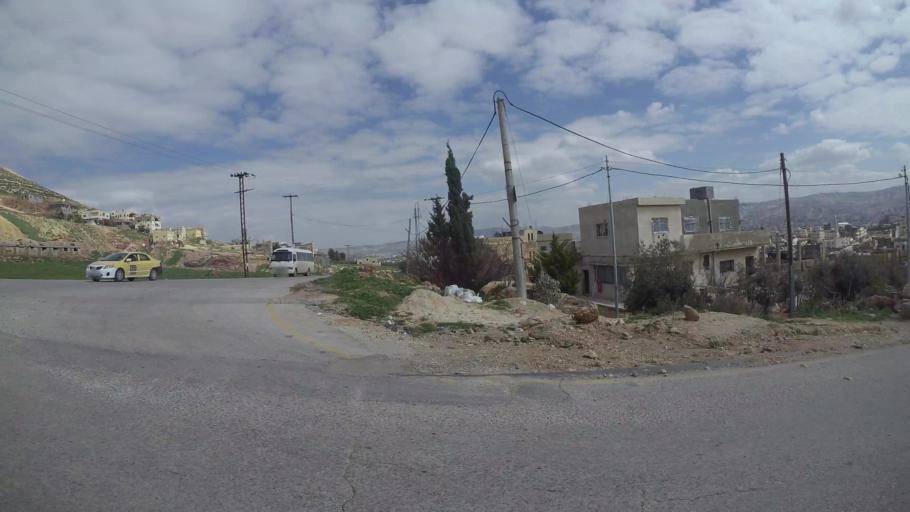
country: JO
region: Amman
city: Al Jubayhah
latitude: 32.0631
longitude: 35.8082
